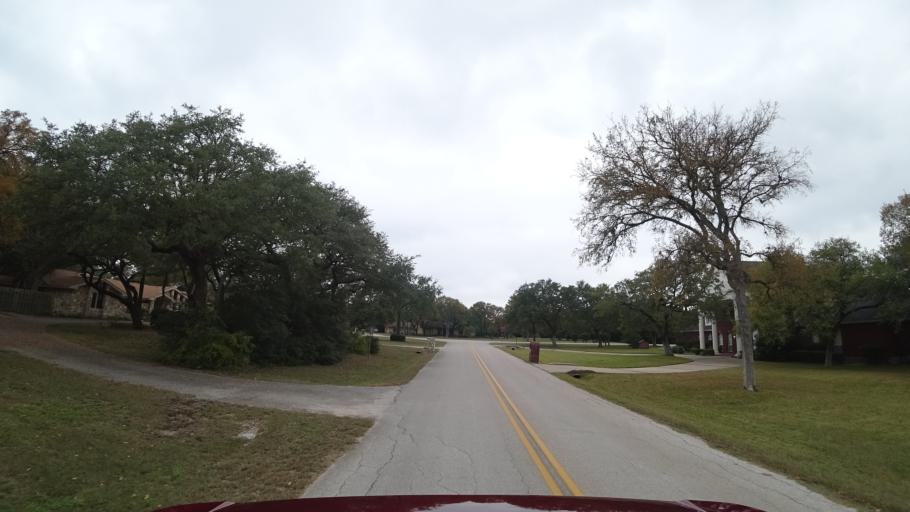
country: US
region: Texas
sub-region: Williamson County
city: Anderson Mill
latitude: 30.4449
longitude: -97.8292
